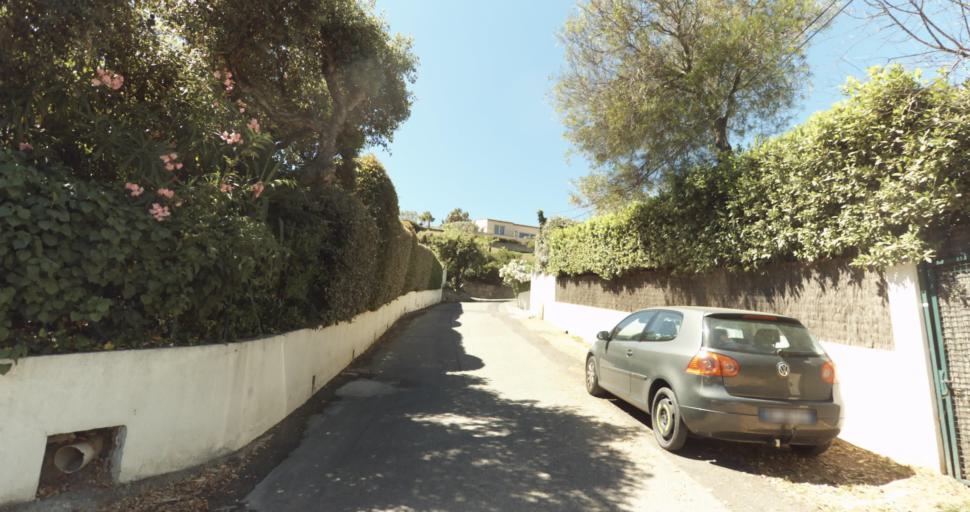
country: FR
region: Provence-Alpes-Cote d'Azur
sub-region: Departement du Var
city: Saint-Tropez
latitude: 43.2618
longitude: 6.6055
